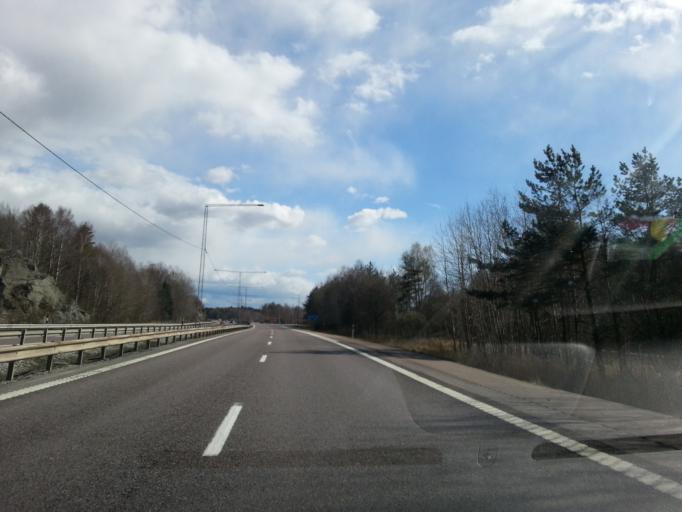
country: SE
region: Vaestra Goetaland
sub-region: Kungalvs Kommun
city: Kode
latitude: 57.9506
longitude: 11.8518
